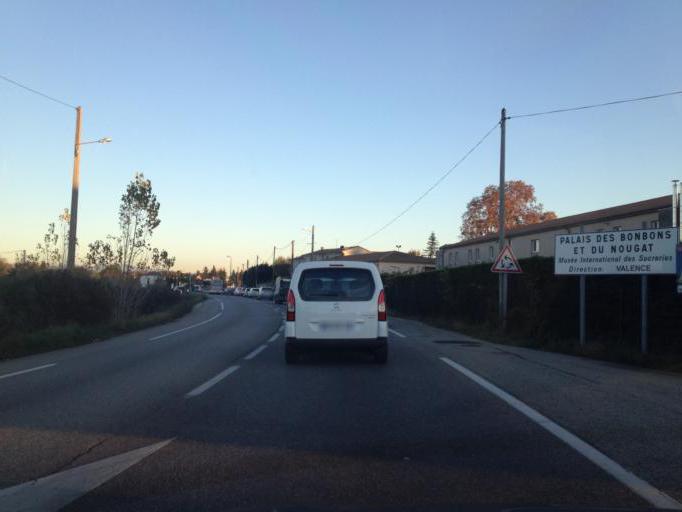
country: FR
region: Rhone-Alpes
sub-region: Departement de la Drome
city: Ancone
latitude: 44.5696
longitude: 4.7293
